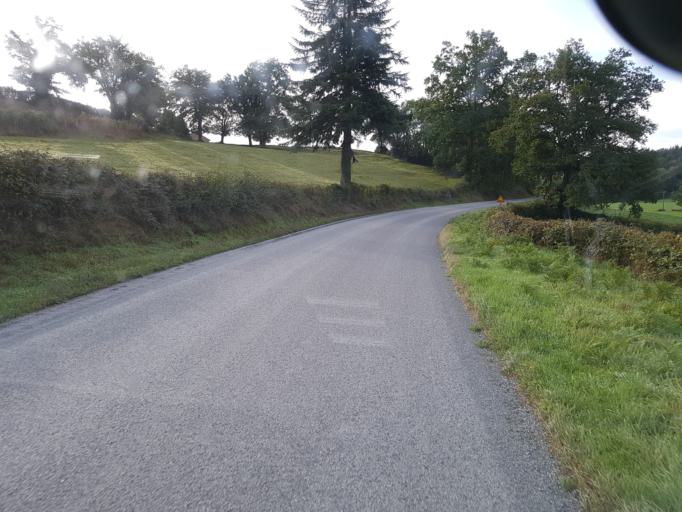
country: FR
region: Bourgogne
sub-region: Departement de Saone-et-Loire
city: Chauffailles
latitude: 46.2630
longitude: 4.4010
